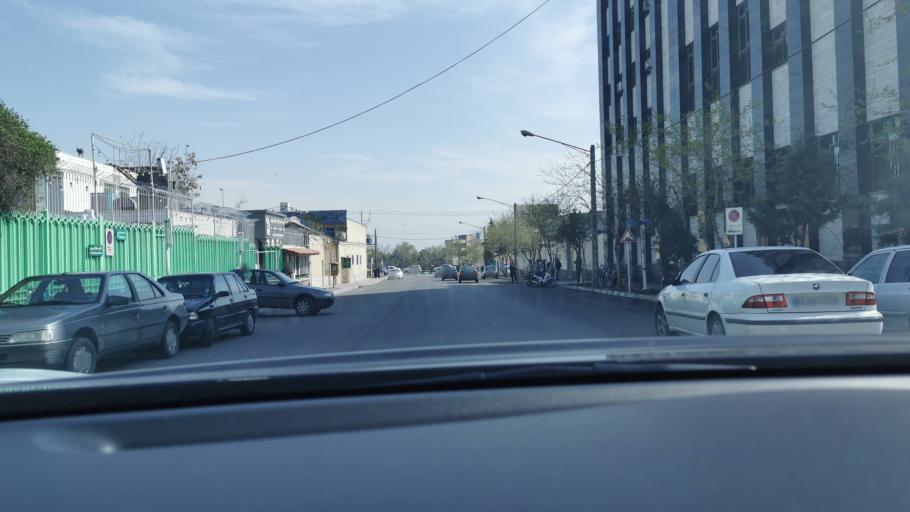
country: IR
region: Razavi Khorasan
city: Mashhad
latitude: 36.2817
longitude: 59.5506
